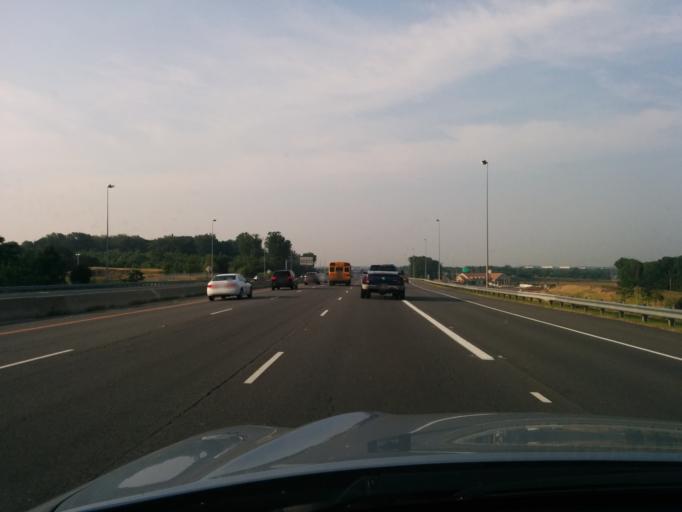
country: US
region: Virginia
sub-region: Loudoun County
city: Dulles Town Center
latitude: 39.0358
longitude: -77.4314
